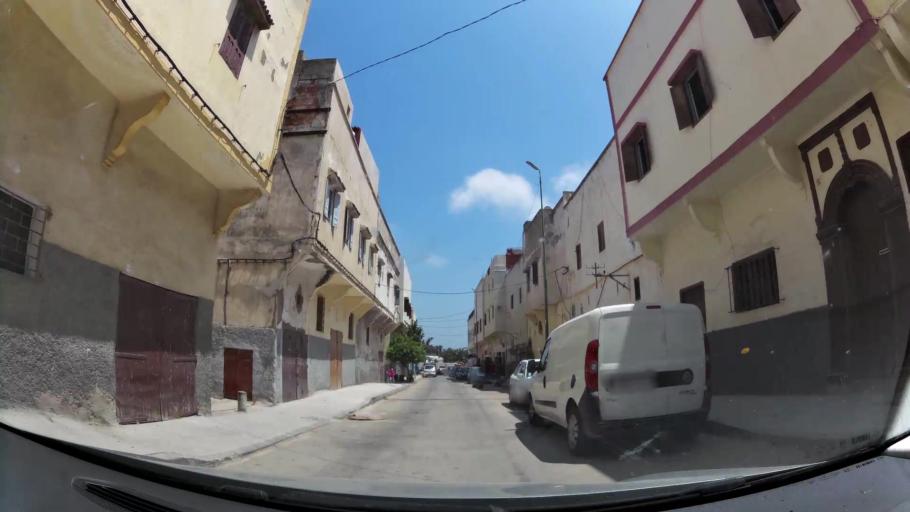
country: MA
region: Rabat-Sale-Zemmour-Zaer
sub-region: Rabat
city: Rabat
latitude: 34.0088
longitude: -6.8622
